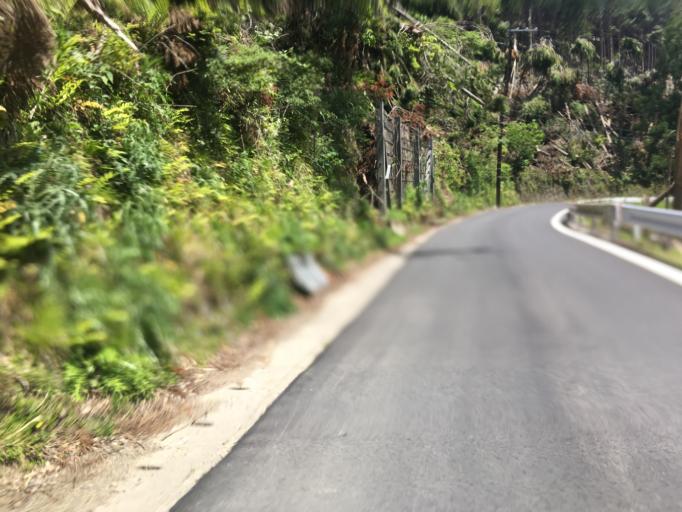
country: JP
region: Kyoto
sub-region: Kyoto-shi
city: Kamigyo-ku
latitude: 35.1004
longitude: 135.7415
